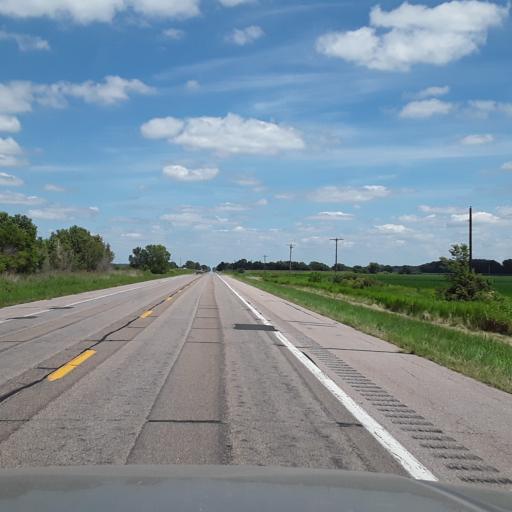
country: US
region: Nebraska
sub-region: Polk County
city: Osceola
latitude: 41.3556
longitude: -97.5695
